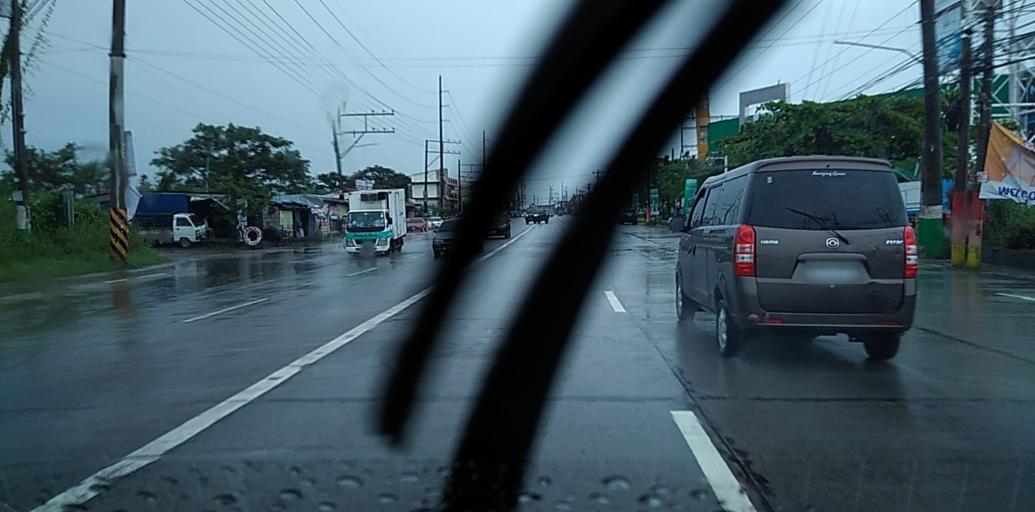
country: PH
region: Central Luzon
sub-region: Province of Pampanga
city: Del Pilar
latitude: 15.0516
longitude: 120.7045
